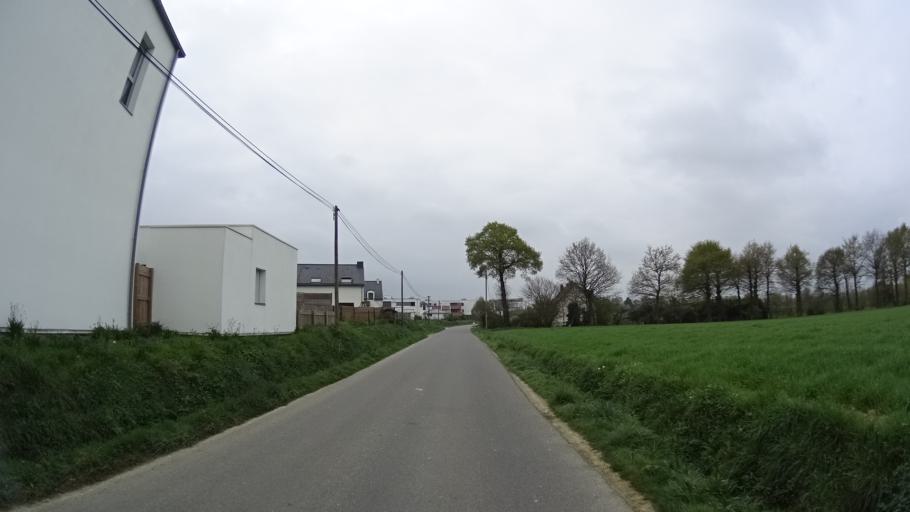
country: FR
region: Brittany
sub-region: Departement d'Ille-et-Vilaine
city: Saint-Gilles
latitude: 48.1508
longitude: -1.8424
